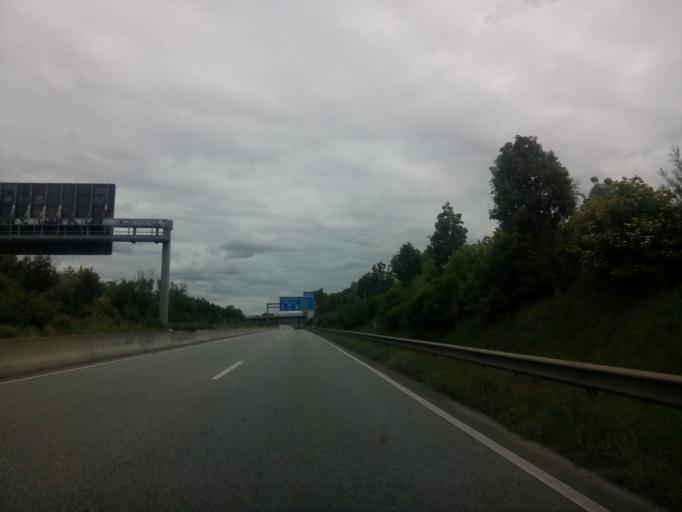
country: DE
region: Lower Saxony
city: Stuhr
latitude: 53.0730
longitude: 8.7652
